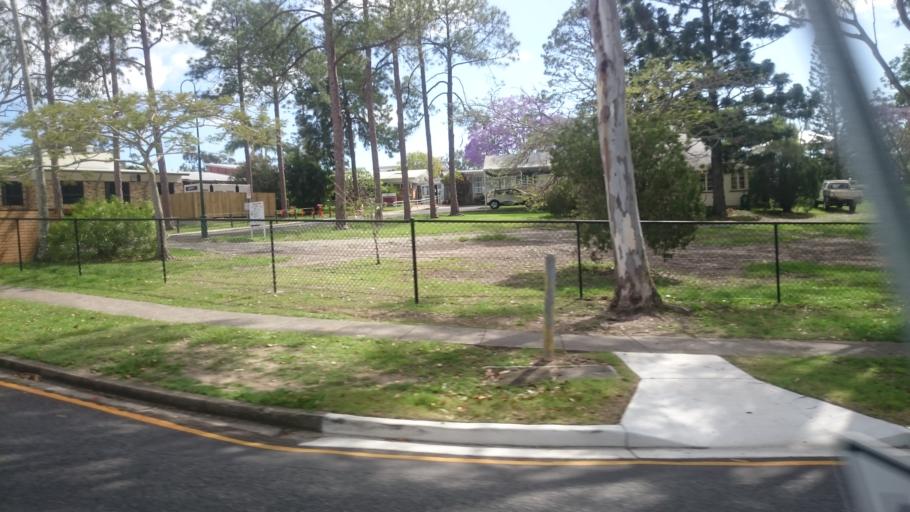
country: AU
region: Queensland
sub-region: Brisbane
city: Manly West
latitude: -27.4635
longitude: 153.1884
